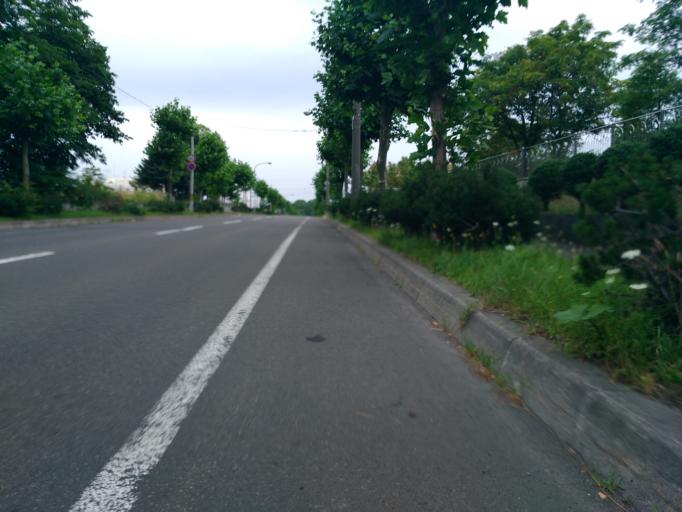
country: JP
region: Hokkaido
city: Ebetsu
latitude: 43.0658
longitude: 141.5024
